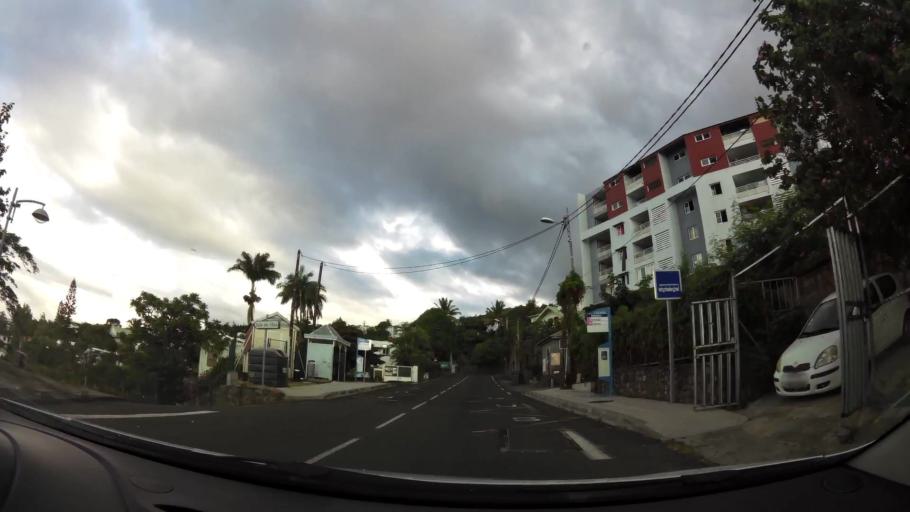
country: RE
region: Reunion
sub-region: Reunion
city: Saint-Denis
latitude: -20.8966
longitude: 55.4466
